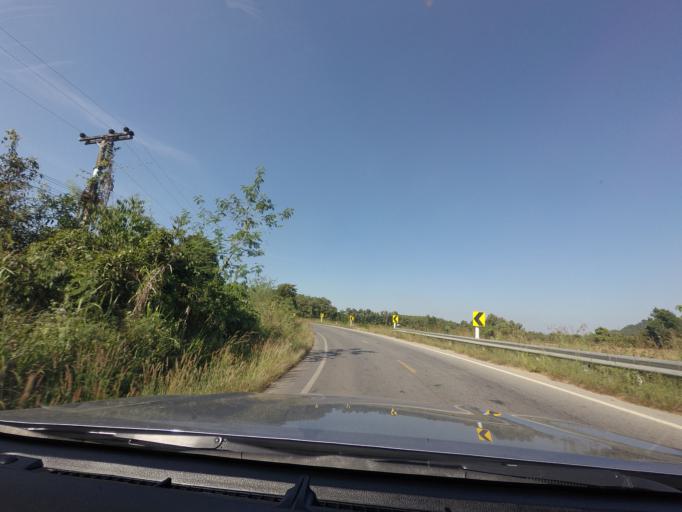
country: TH
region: Sukhothai
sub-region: Amphoe Si Satchanalai
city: Si Satchanalai
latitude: 17.7025
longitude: 99.6949
